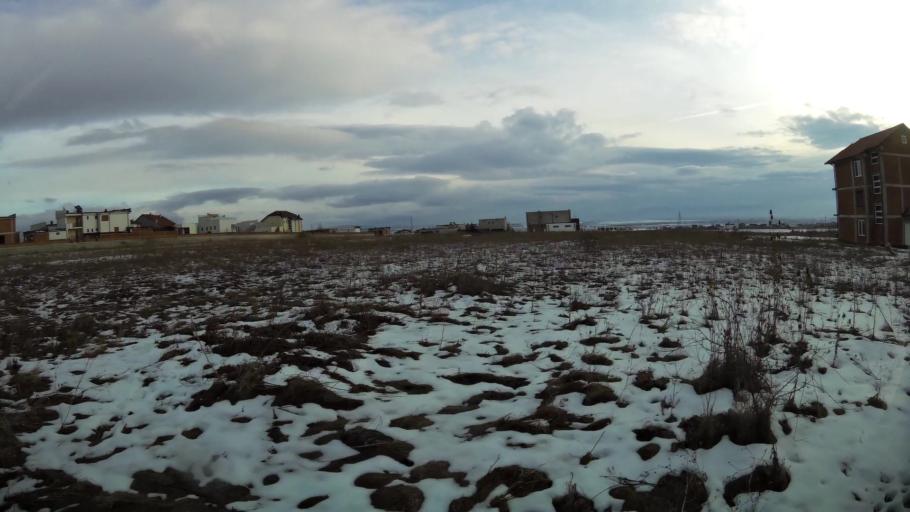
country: XK
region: Pristina
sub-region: Komuna e Prishtines
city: Pristina
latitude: 42.6245
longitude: 21.1585
